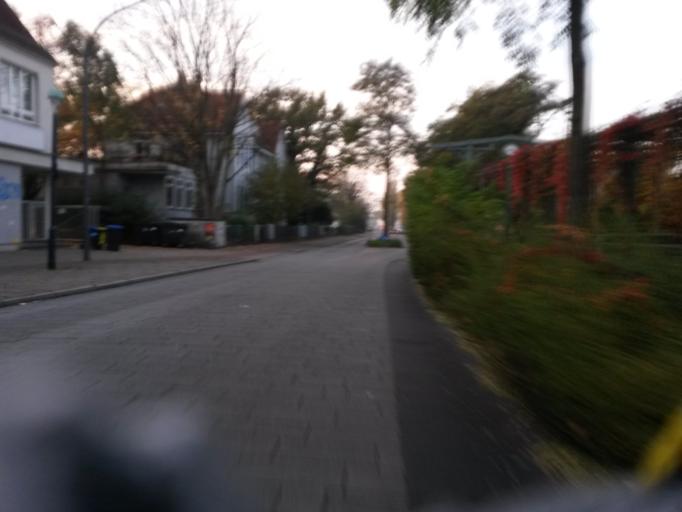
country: DE
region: Lower Saxony
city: Lilienthal
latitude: 53.0618
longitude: 8.8861
